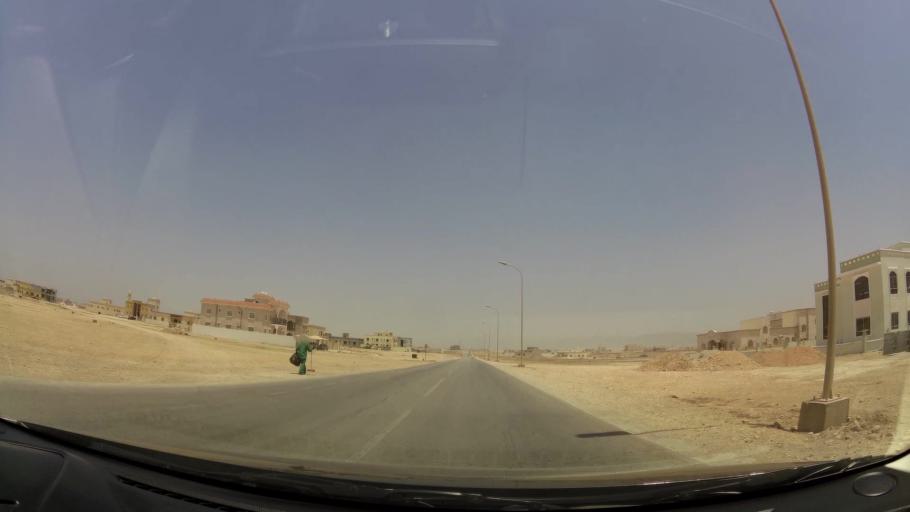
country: OM
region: Zufar
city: Salalah
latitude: 17.0918
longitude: 54.2047
